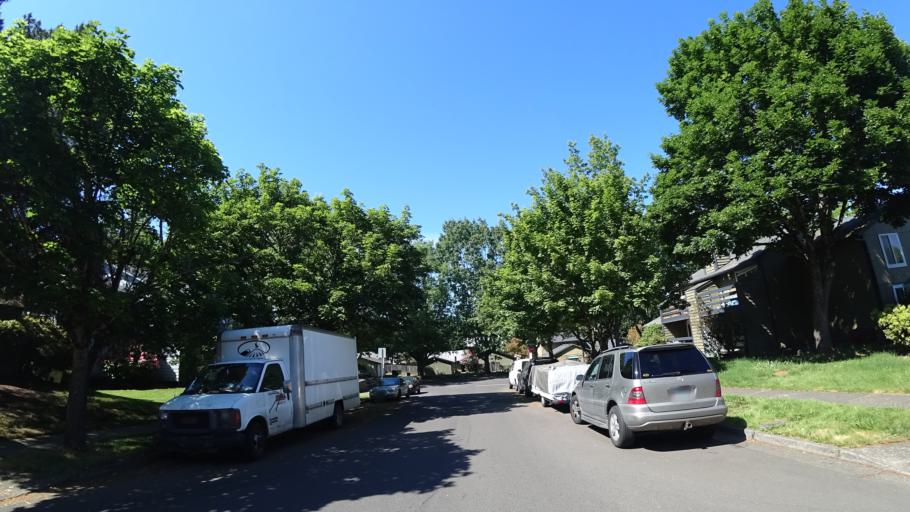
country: US
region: Oregon
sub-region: Washington County
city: Beaverton
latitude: 45.4504
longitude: -122.8035
